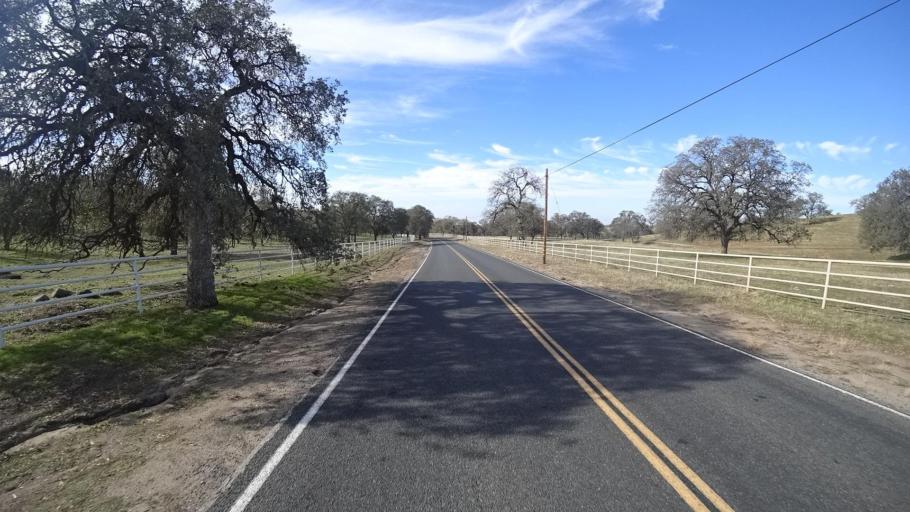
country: US
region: California
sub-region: Kern County
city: Alta Sierra
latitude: 35.6293
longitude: -118.8200
